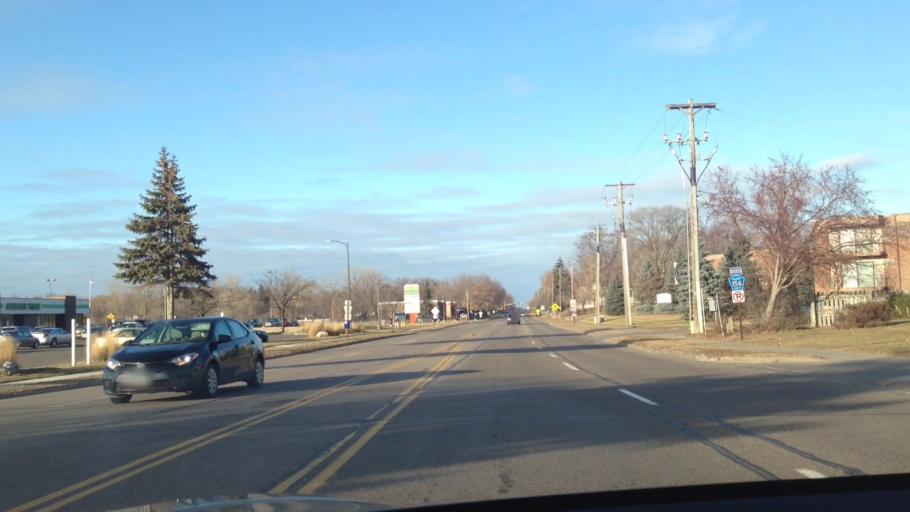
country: US
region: Minnesota
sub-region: Hennepin County
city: New Hope
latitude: 45.0334
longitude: -93.3803
